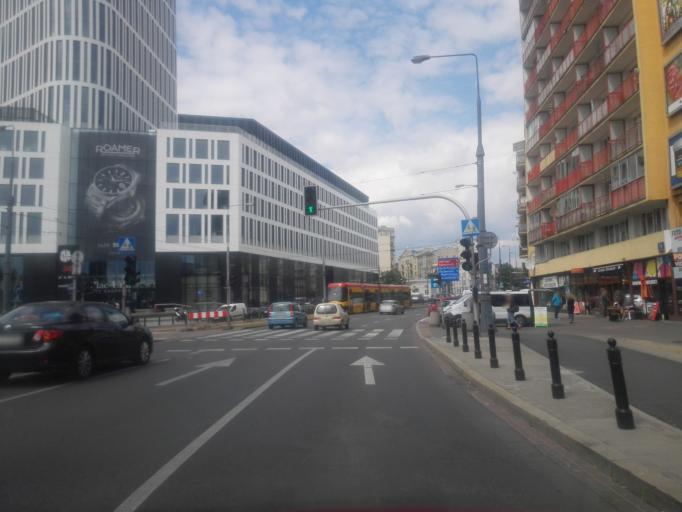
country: PL
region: Masovian Voivodeship
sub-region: Warszawa
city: Srodmiescie
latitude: 52.2116
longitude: 21.0208
